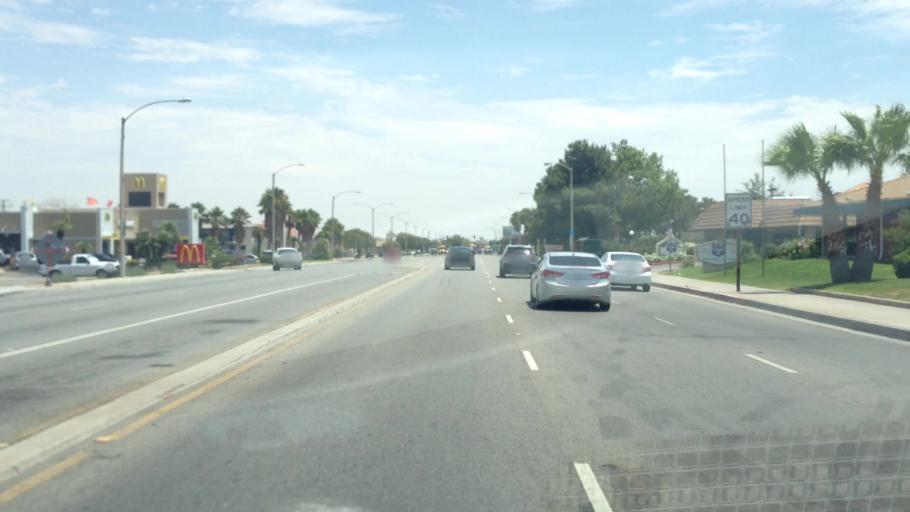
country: US
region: California
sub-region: Los Angeles County
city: Palmdale
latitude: 34.5798
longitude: -118.1293
